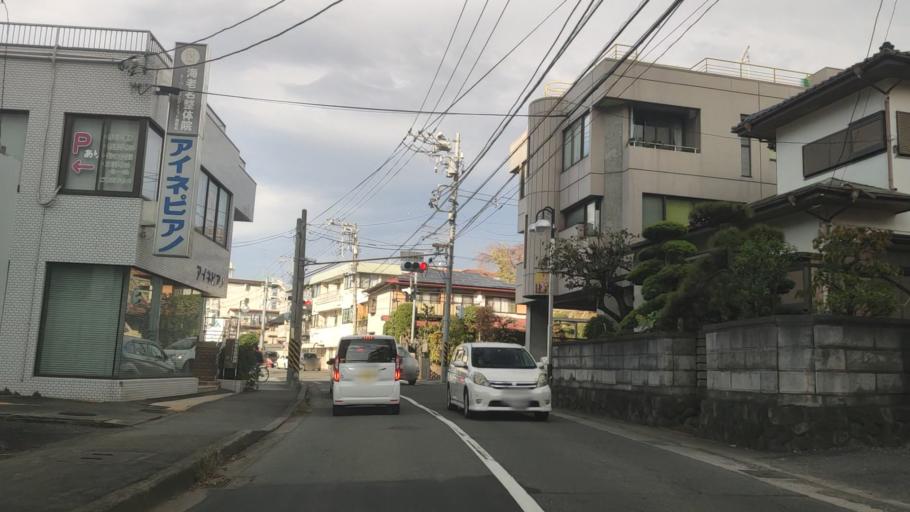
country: JP
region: Kanagawa
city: Zama
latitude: 35.4528
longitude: 139.3971
